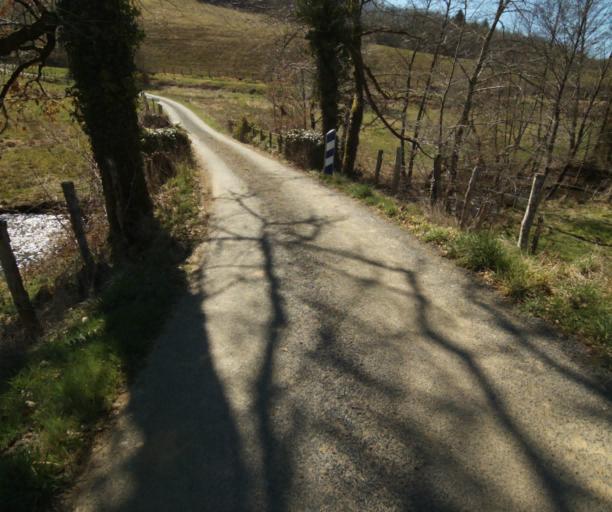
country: FR
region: Limousin
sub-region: Departement de la Correze
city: Chamboulive
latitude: 45.4500
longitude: 1.6812
